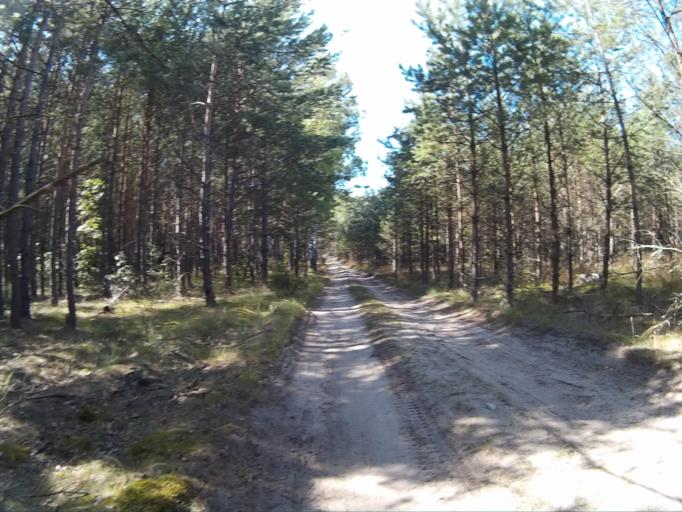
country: PL
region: Pomeranian Voivodeship
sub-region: Powiat chojnicki
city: Czersk
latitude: 53.7233
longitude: 17.9015
